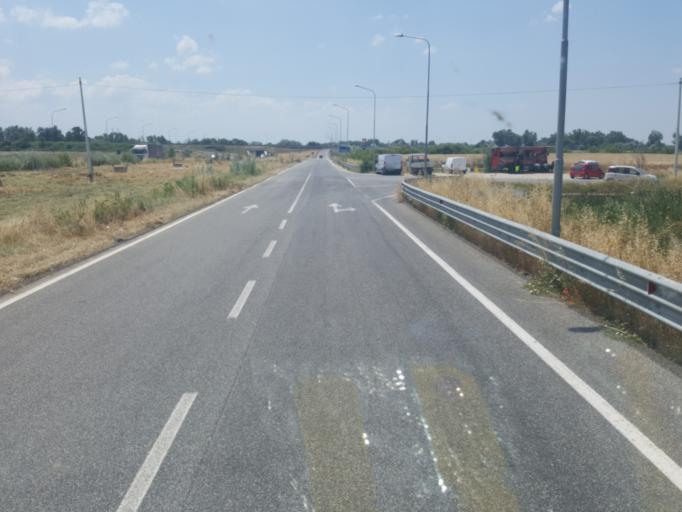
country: IT
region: Latium
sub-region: Citta metropolitana di Roma Capitale
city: Fiano Romano
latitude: 42.1578
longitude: 12.6427
